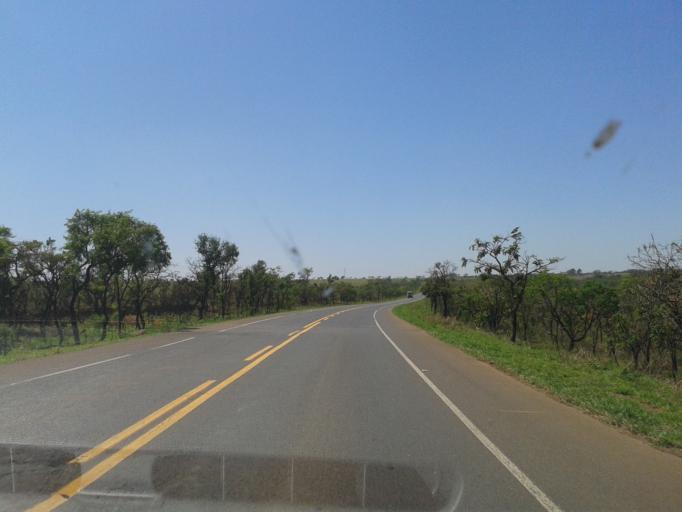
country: BR
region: Minas Gerais
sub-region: Patrocinio
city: Patrocinio
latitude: -19.2847
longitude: -47.4128
